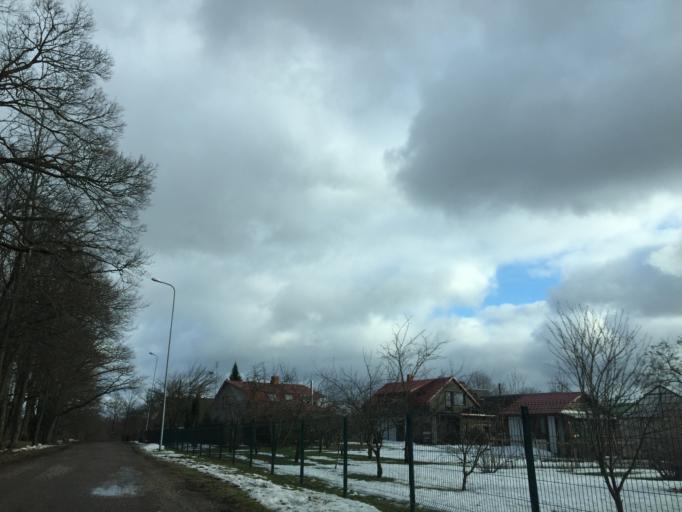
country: LV
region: Aloja
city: Aloja
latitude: 57.7719
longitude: 24.8166
